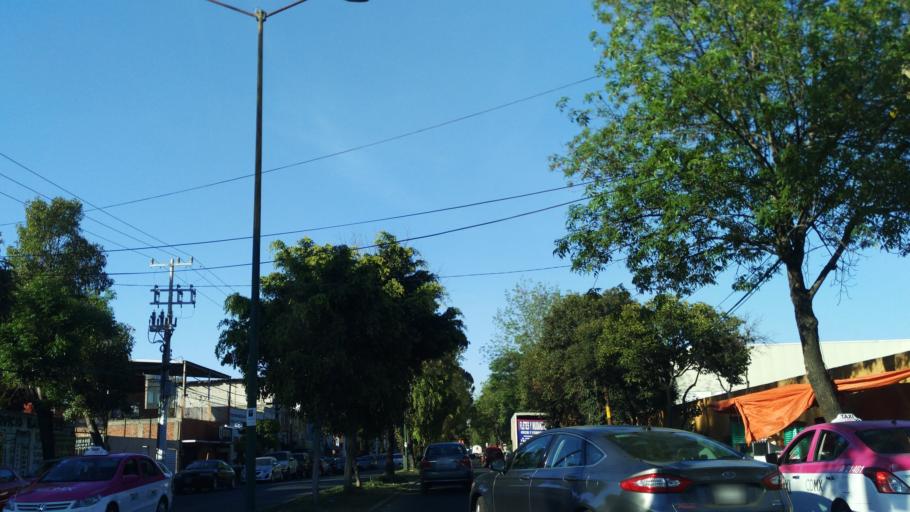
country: MX
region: Mexico City
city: Xochimilco
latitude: 19.2943
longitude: -99.1103
